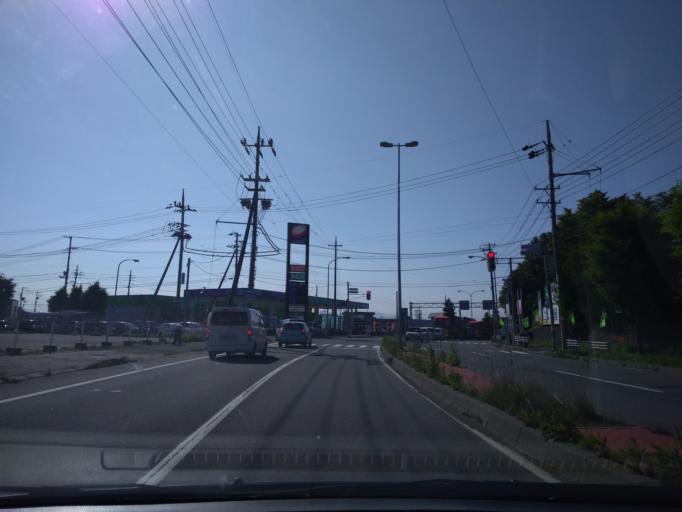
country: JP
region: Hokkaido
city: Kitahiroshima
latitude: 42.9796
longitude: 141.4856
